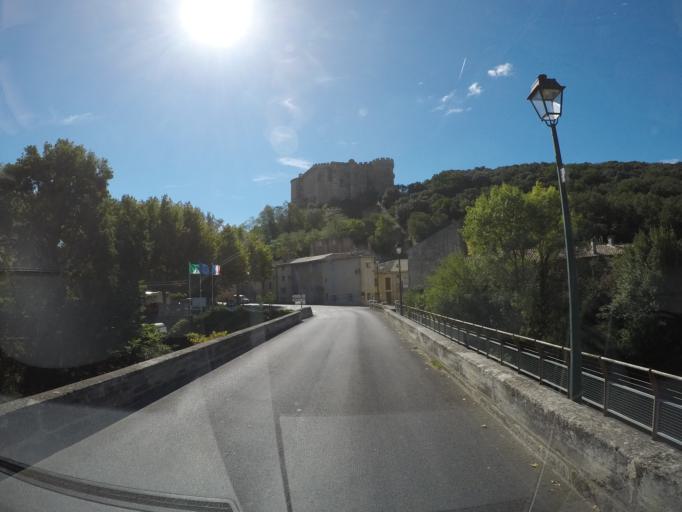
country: FR
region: Rhone-Alpes
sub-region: Departement de la Drome
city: Suze-la-Rousse
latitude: 44.2918
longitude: 4.8383
